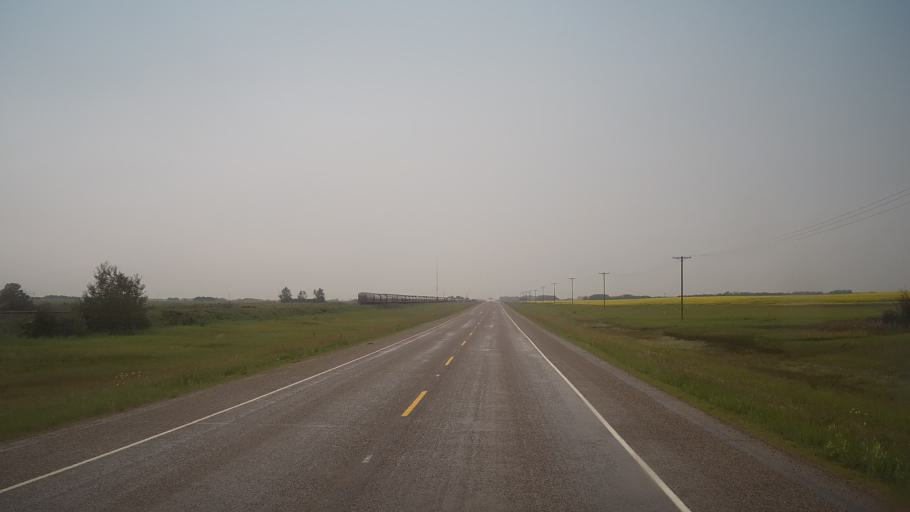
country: CA
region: Saskatchewan
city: Biggar
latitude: 52.1649
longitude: -108.2990
